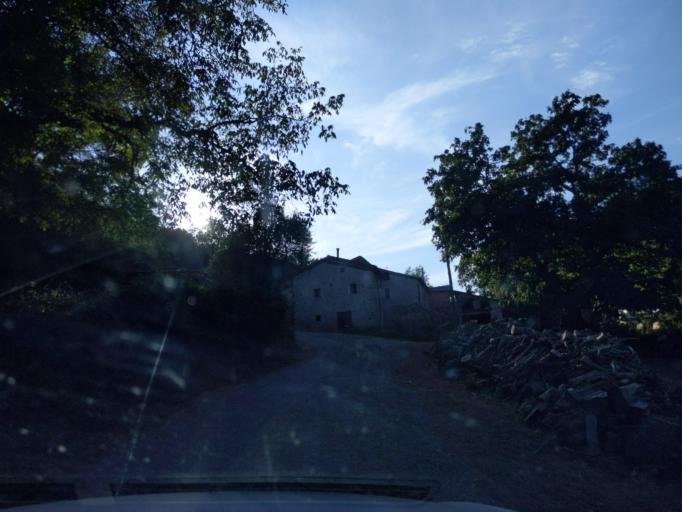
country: ES
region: La Rioja
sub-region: Provincia de La Rioja
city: Ojacastro
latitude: 42.3752
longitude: -3.0017
